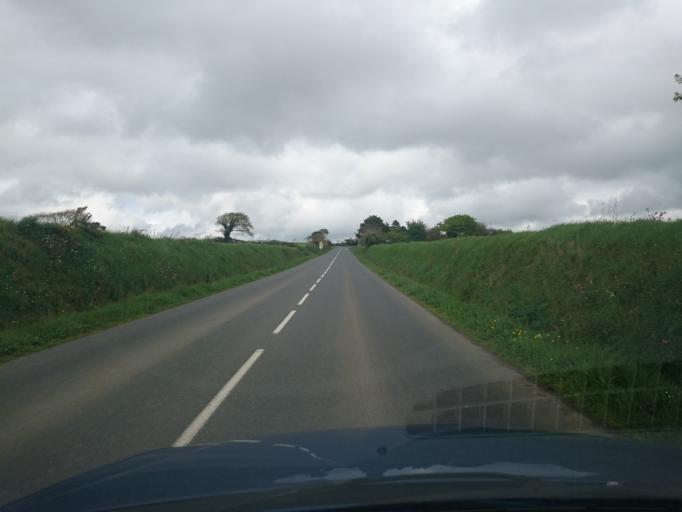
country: FR
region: Brittany
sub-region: Departement du Finistere
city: Plouvien
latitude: 48.5369
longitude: -4.4265
